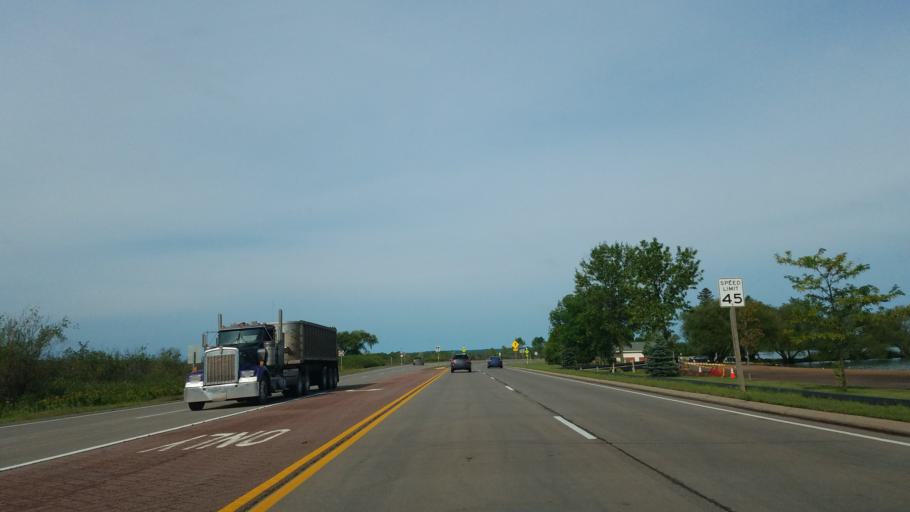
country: US
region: Wisconsin
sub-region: Ashland County
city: Ashland
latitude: 46.5826
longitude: -90.9169
